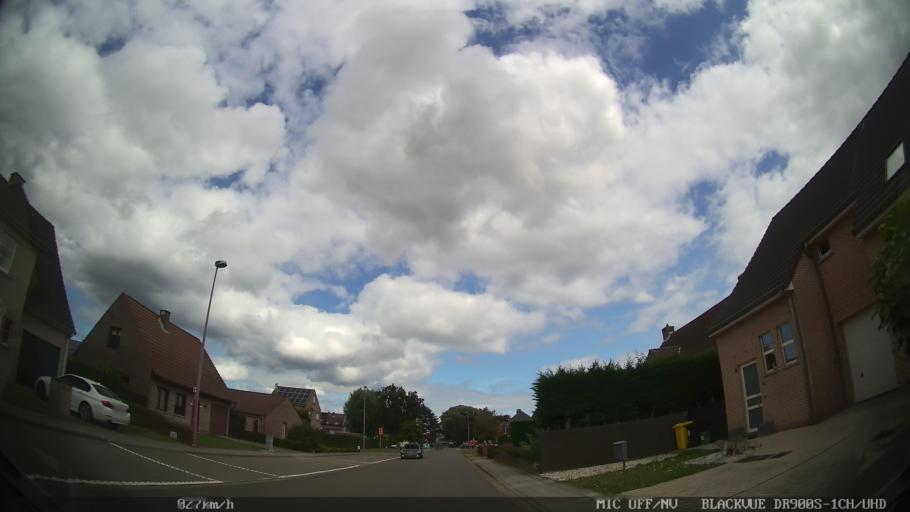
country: BE
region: Flanders
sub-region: Provincie Antwerpen
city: Stabroek
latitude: 51.3295
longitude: 4.3753
